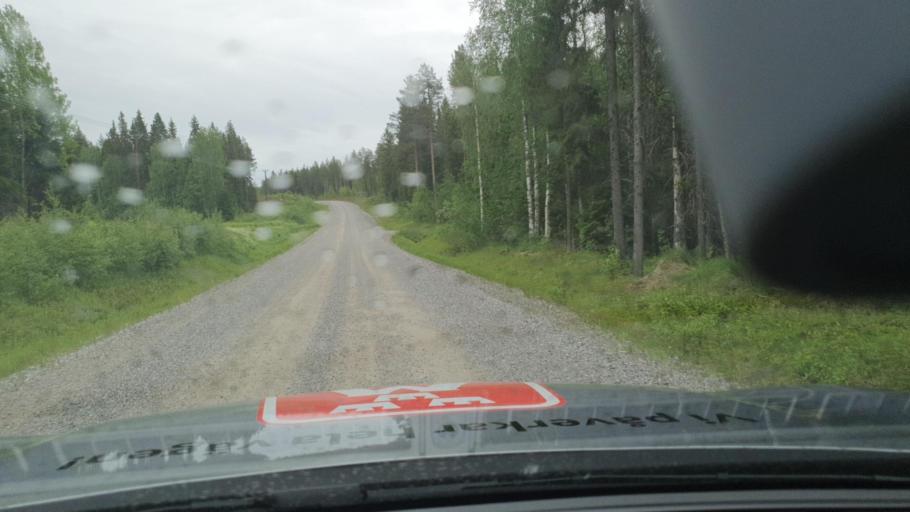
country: SE
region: Norrbotten
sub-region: Kalix Kommun
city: Rolfs
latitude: 66.0135
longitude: 23.1208
